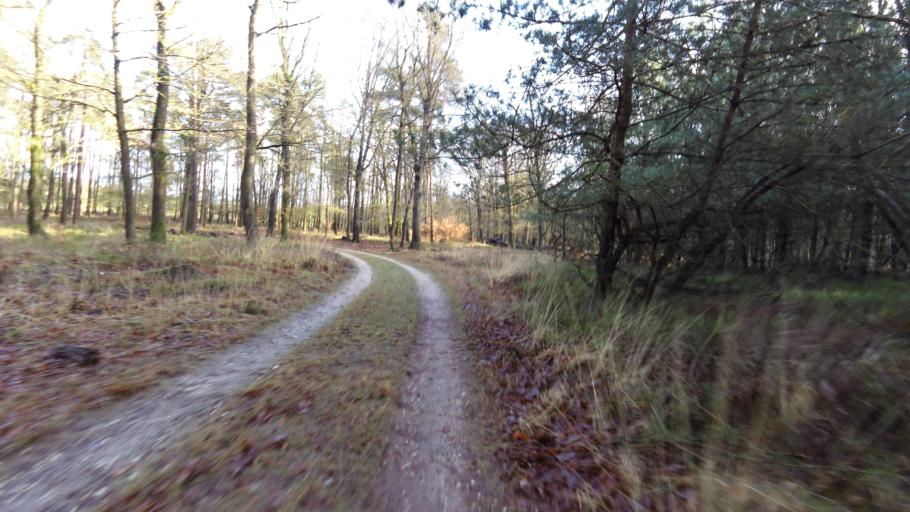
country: NL
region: Gelderland
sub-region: Gemeente Apeldoorn
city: Apeldoorn
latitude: 52.2360
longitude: 5.8844
